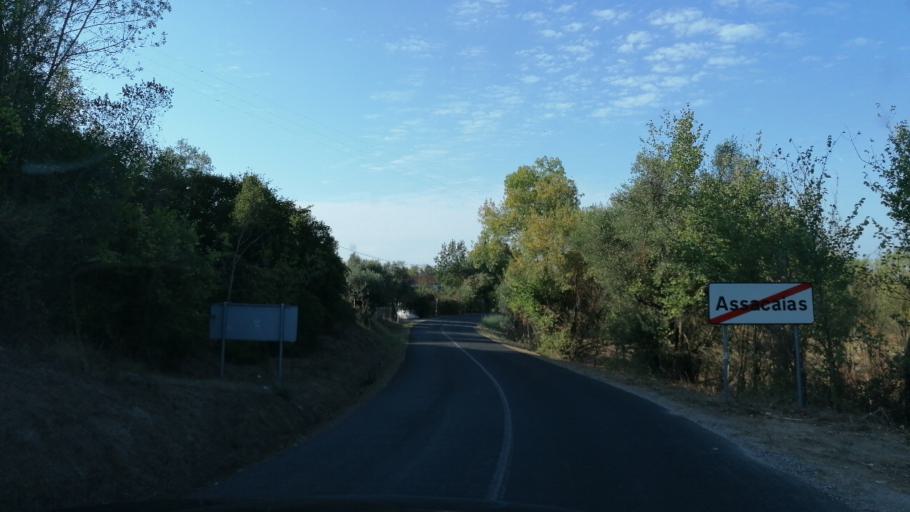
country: PT
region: Santarem
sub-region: Santarem
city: Santarem
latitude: 39.2632
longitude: -8.6651
